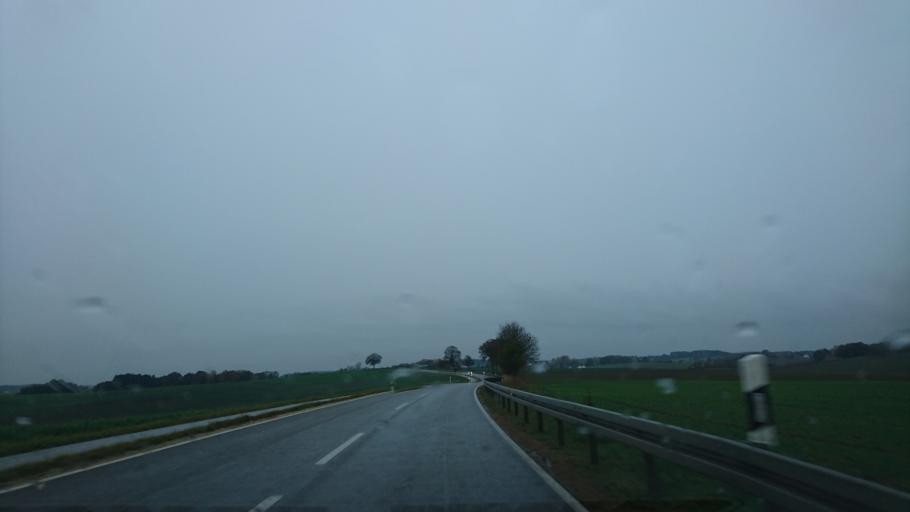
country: DE
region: Bavaria
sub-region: Upper Bavaria
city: Hilgertshausen-Tandern
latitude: 48.4321
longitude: 11.3395
